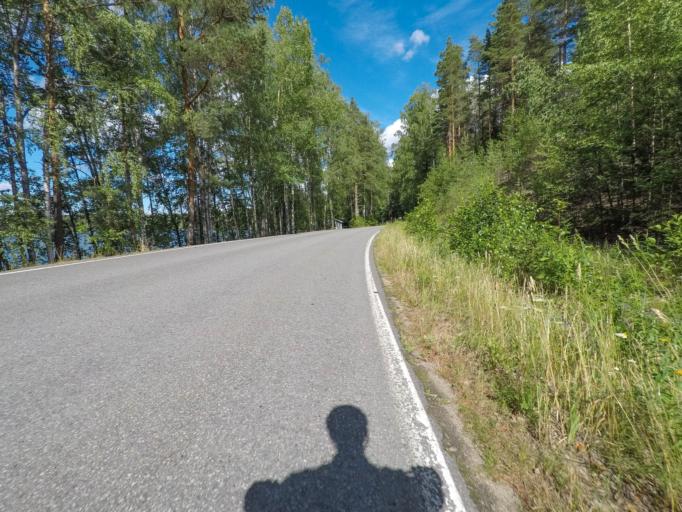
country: FI
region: South Karelia
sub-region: Lappeenranta
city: Joutseno
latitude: 61.1179
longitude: 28.3766
